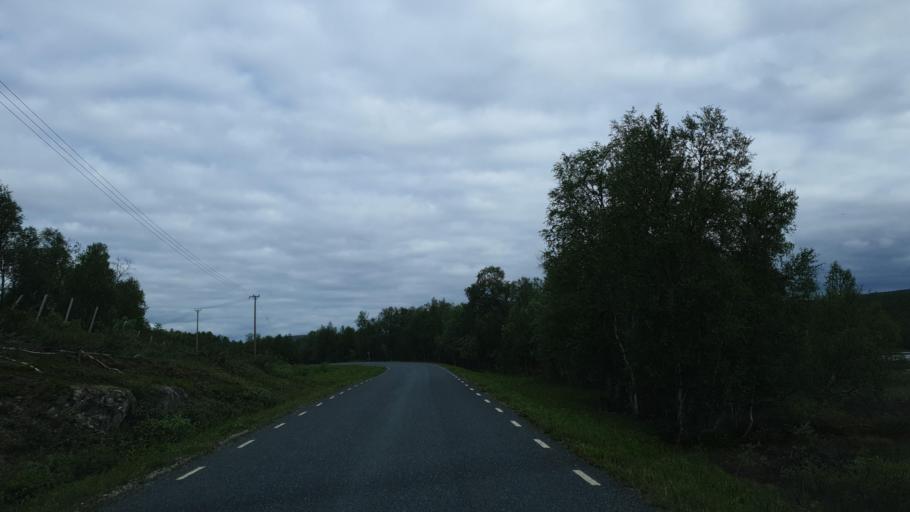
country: NO
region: Nordland
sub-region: Hattfjelldal
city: Hattfjelldal
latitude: 65.4178
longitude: 14.7758
